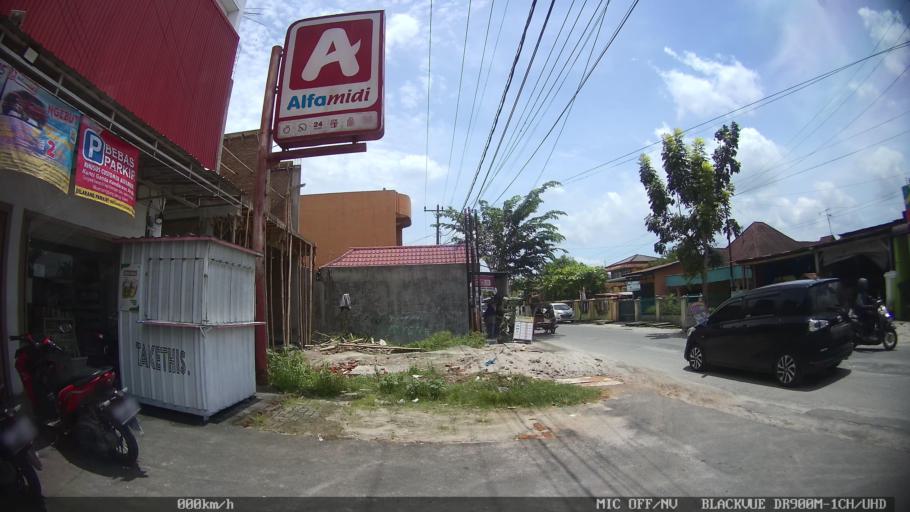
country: ID
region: North Sumatra
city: Percut
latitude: 3.5576
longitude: 98.8749
